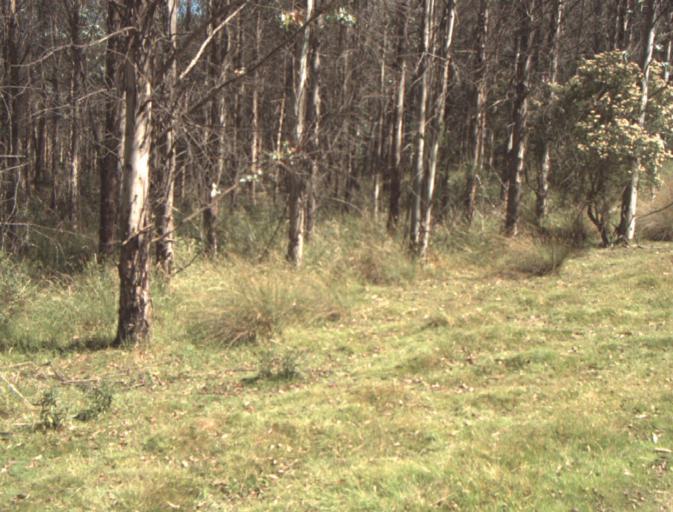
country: AU
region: Tasmania
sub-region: Dorset
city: Scottsdale
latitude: -41.2677
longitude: 147.3518
